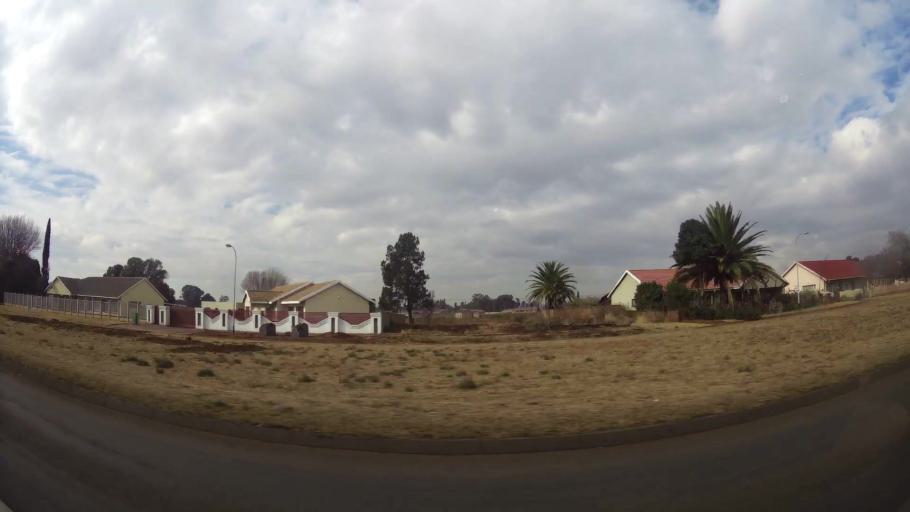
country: ZA
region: Gauteng
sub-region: Sedibeng District Municipality
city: Meyerton
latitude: -26.5895
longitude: 28.0017
